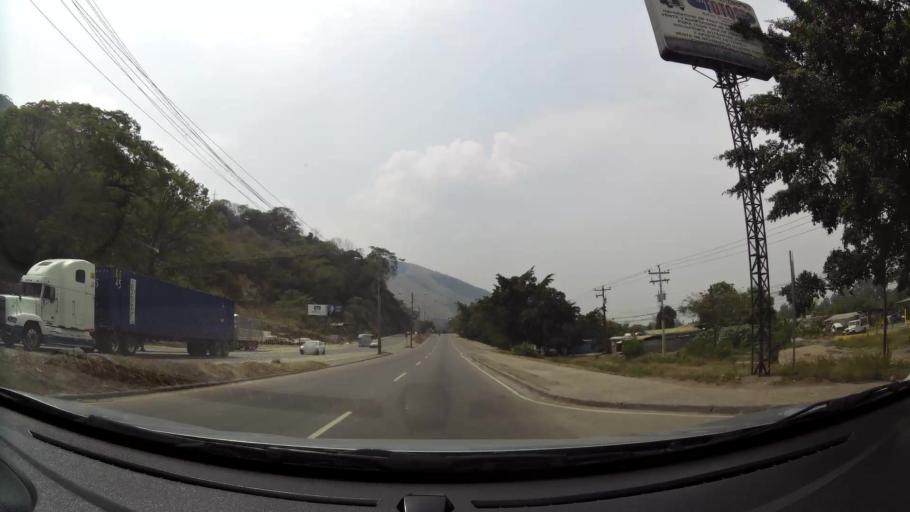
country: HN
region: Cortes
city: Chotepe
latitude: 15.4199
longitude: -88.0181
